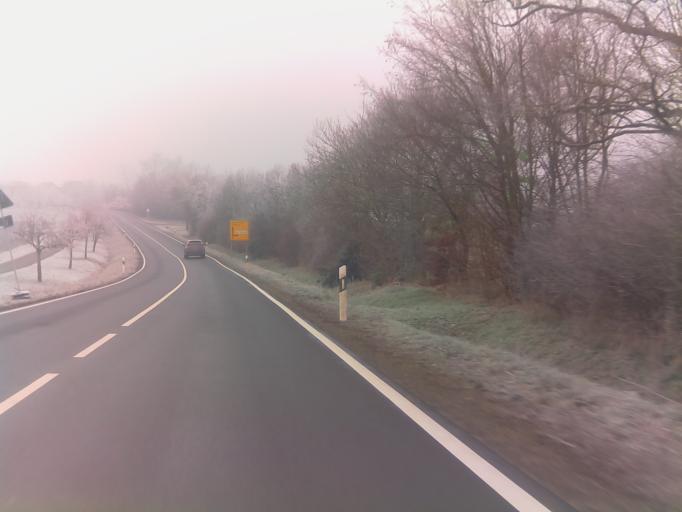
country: DE
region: Bavaria
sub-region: Regierungsbezirk Unterfranken
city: Wonfurt
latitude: 50.0173
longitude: 10.4759
